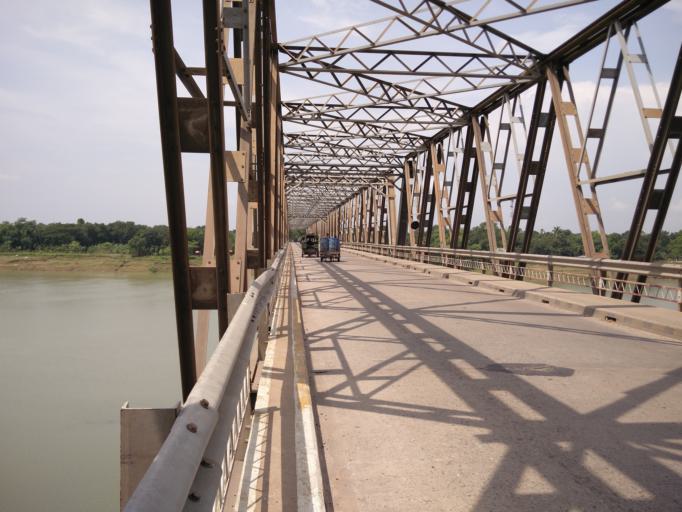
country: BD
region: Khulna
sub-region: Magura
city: Magura
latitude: 23.5415
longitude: 89.5169
